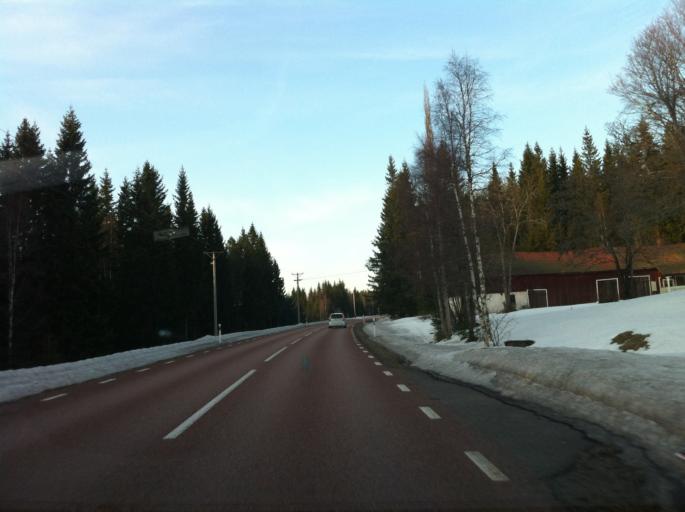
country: SE
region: Dalarna
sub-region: Vansbro Kommun
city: Vansbro
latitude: 60.2692
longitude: 14.1717
